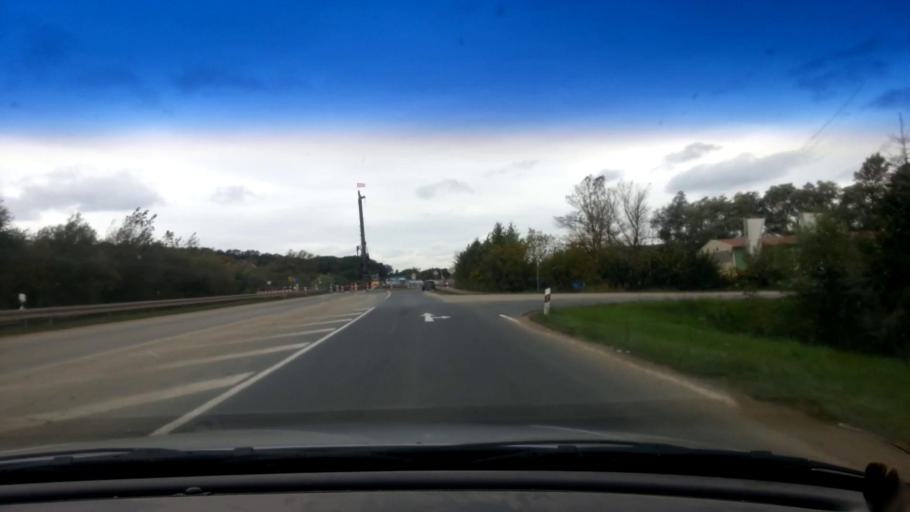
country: DE
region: Bavaria
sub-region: Upper Franconia
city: Baunach
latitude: 49.9755
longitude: 10.8618
